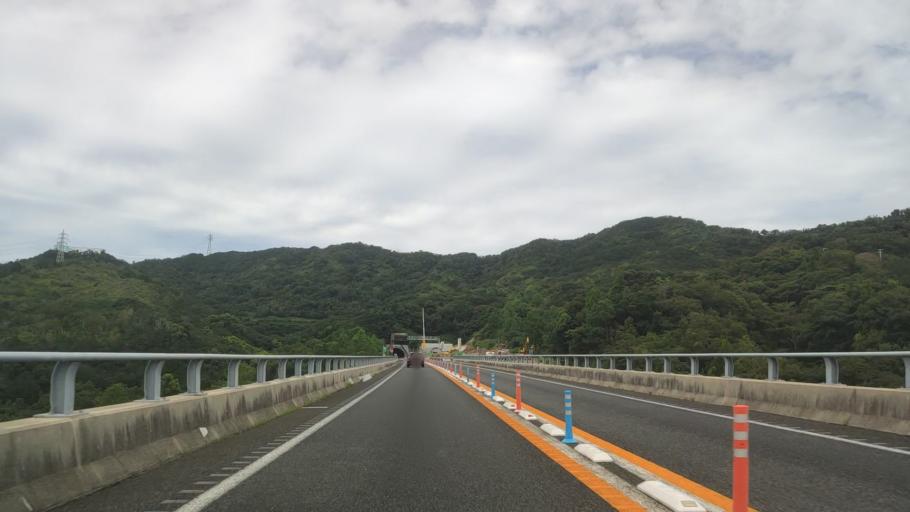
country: JP
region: Wakayama
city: Gobo
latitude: 33.8456
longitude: 135.2182
